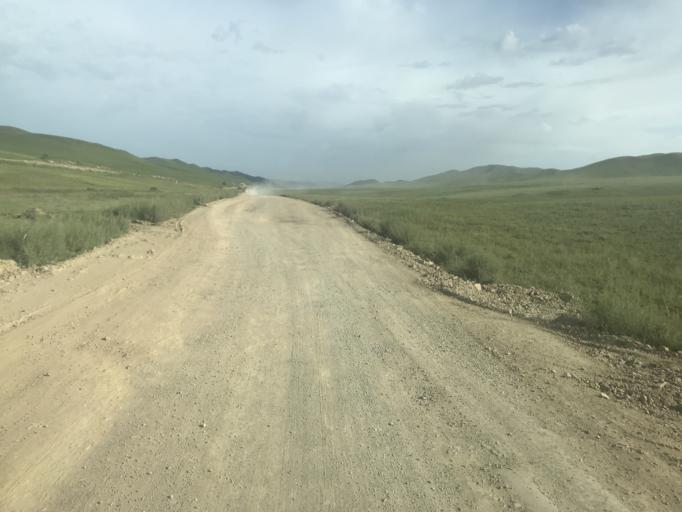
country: MN
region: Central Aimak
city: Javhlant
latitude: 48.7396
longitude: 106.1294
